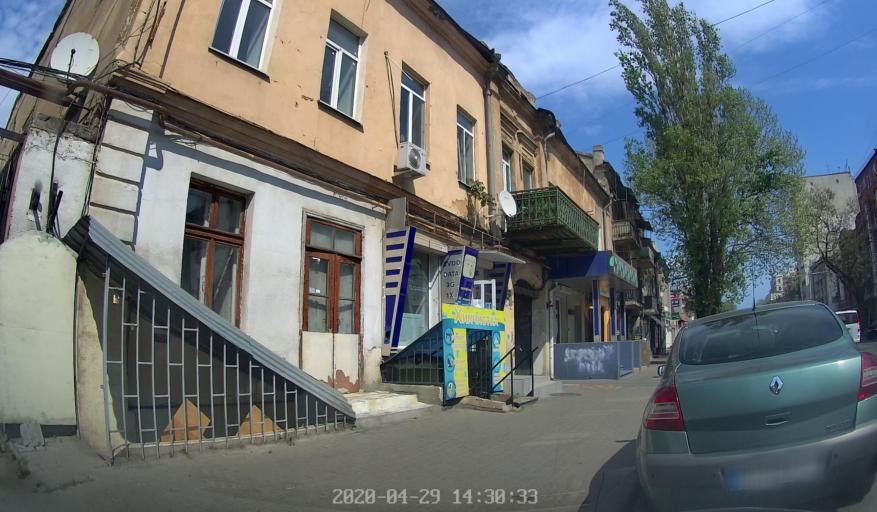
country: NG
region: Niger
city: Lemu
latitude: 9.2943
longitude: 6.1470
